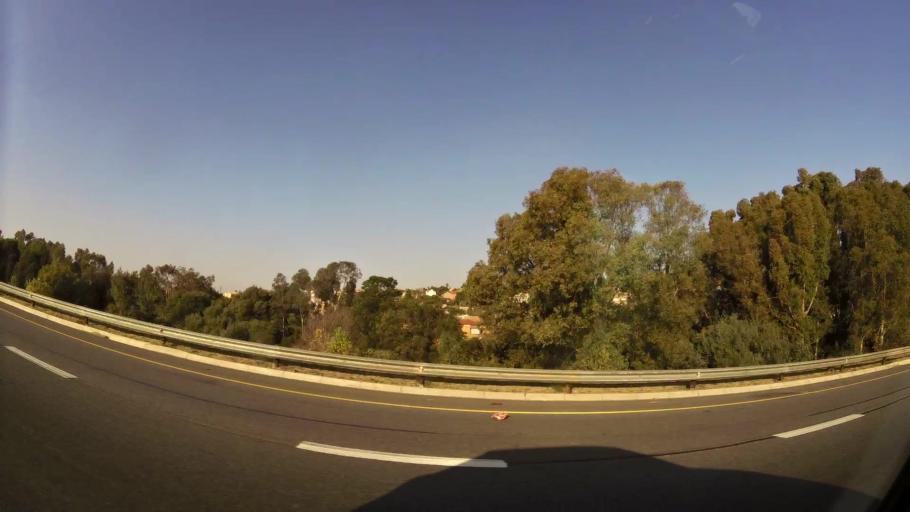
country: ZA
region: Gauteng
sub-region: Ekurhuleni Metropolitan Municipality
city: Germiston
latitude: -26.2469
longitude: 28.1237
